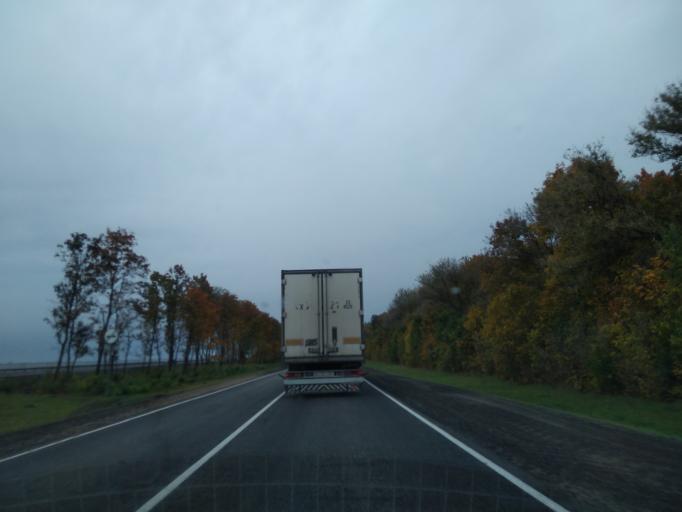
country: RU
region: Lipetsk
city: Zadonsk
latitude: 52.4477
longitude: 38.7830
